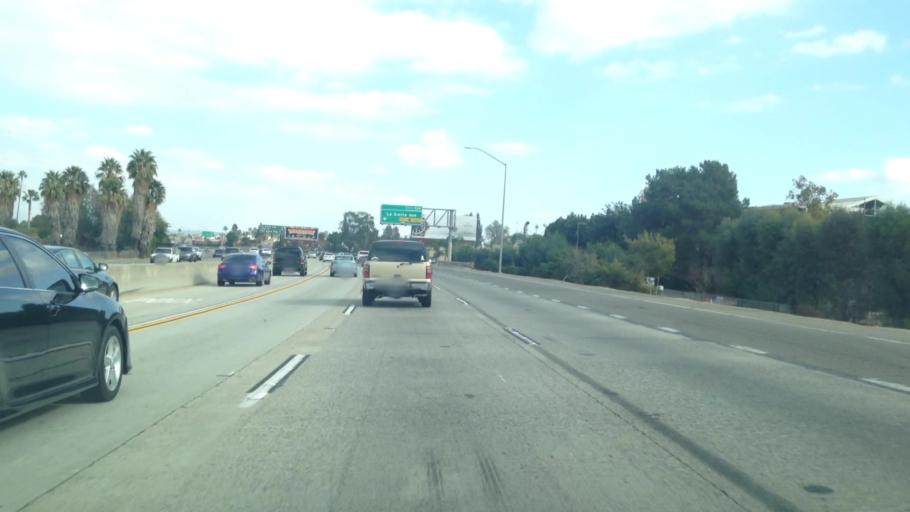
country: US
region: California
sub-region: Riverside County
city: Home Gardens
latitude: 33.8967
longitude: -117.4841
